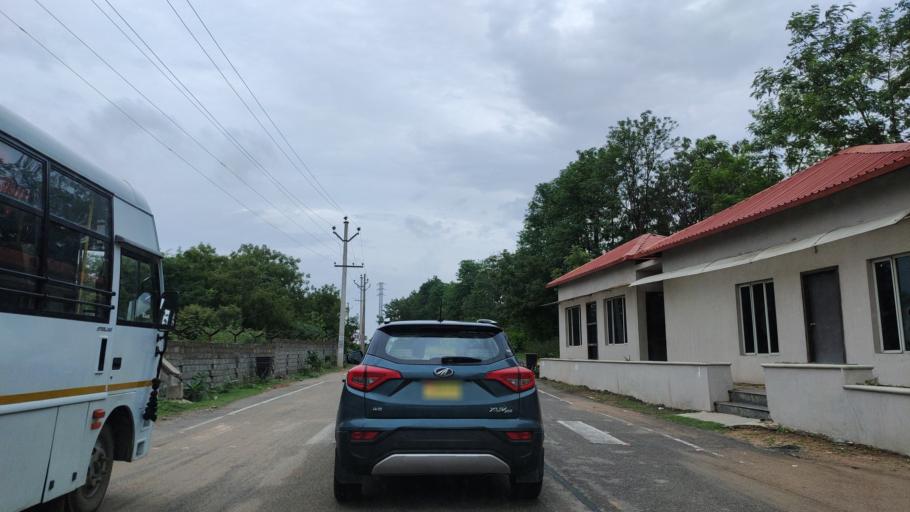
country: IN
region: Telangana
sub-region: Rangareddi
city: Secunderabad
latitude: 17.5775
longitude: 78.6014
